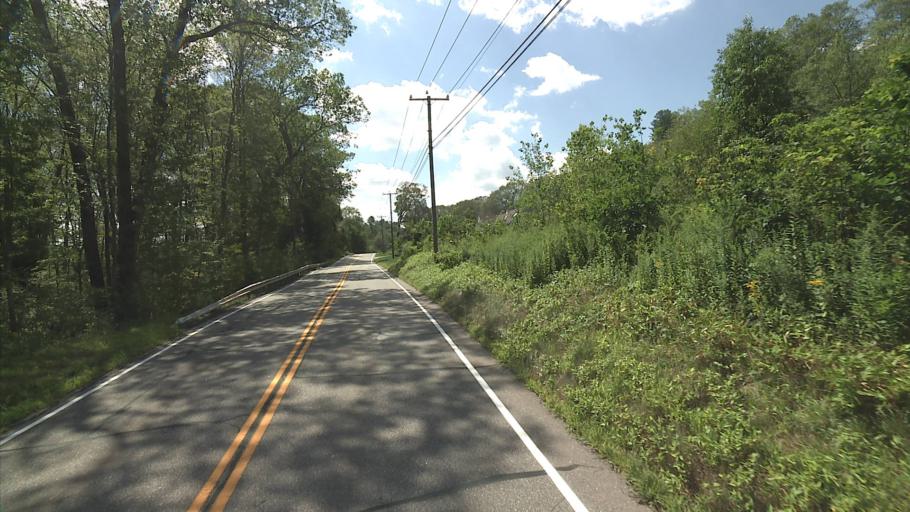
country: US
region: Connecticut
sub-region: Windham County
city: South Woodstock
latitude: 41.8912
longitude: -72.0800
